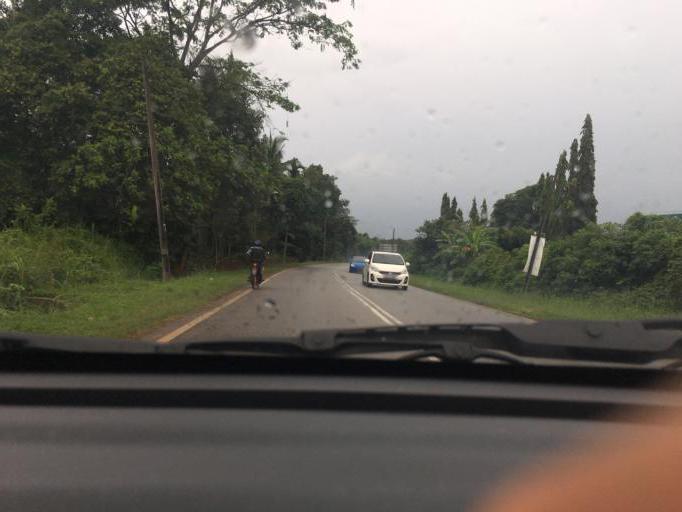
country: MY
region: Kedah
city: Bedong
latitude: 5.7006
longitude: 100.6327
